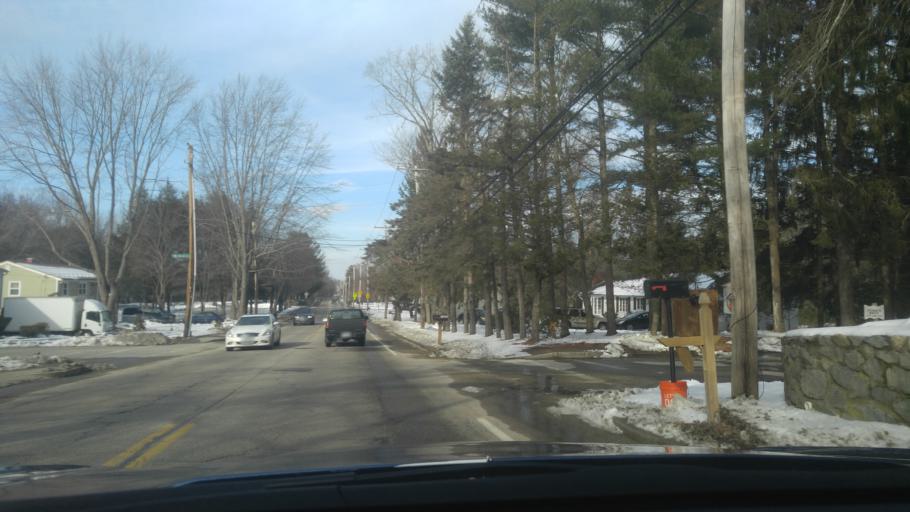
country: US
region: Rhode Island
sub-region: Kent County
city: West Warwick
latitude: 41.6748
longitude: -71.5292
